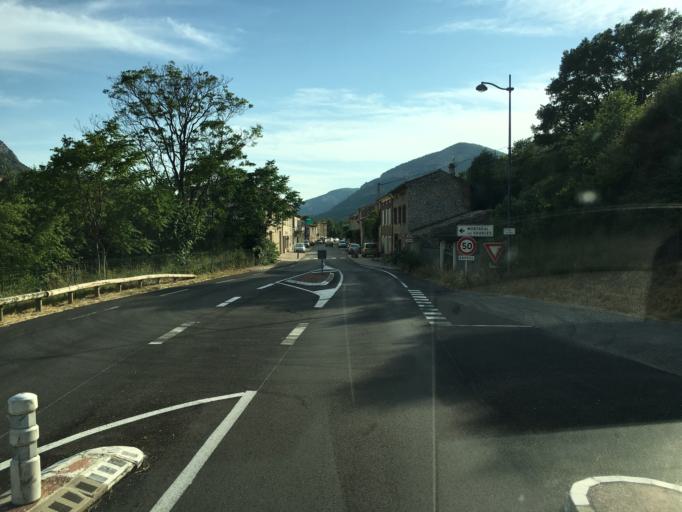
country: FR
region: Rhone-Alpes
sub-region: Departement de la Drome
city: Buis-les-Baronnies
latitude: 44.4153
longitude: 5.2693
